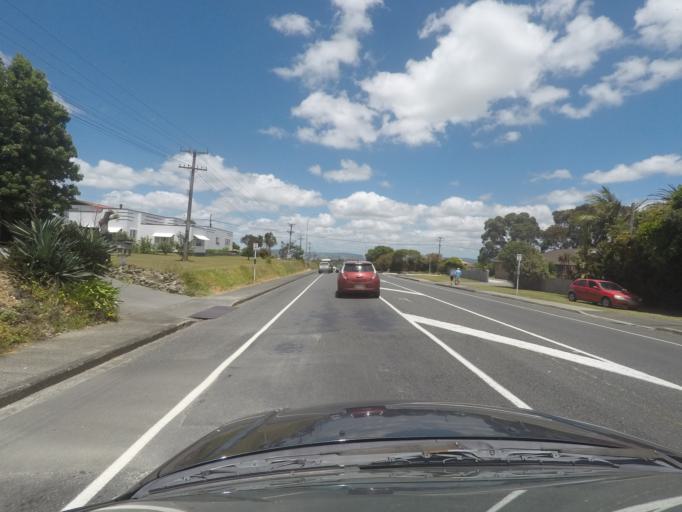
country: NZ
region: Northland
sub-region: Whangarei
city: Whangarei
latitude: -35.7497
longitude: 174.3677
